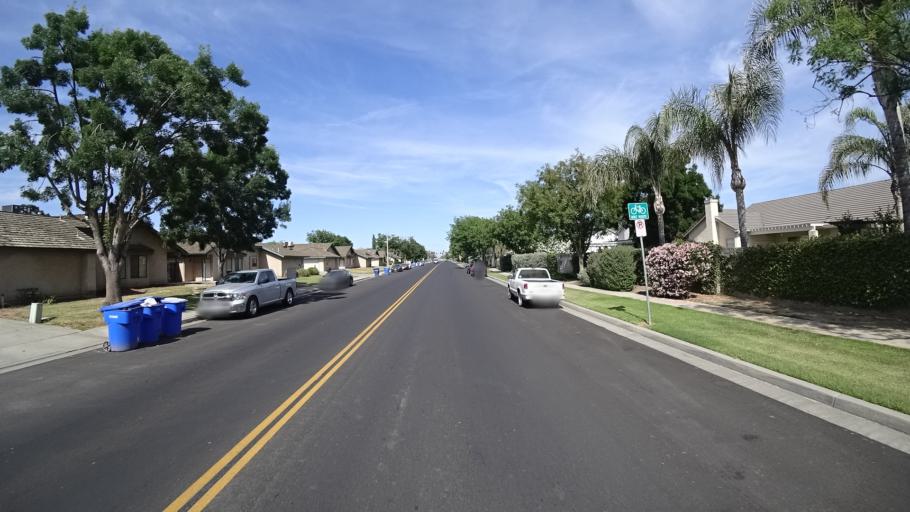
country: US
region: California
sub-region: Kings County
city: Hanford
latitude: 36.3573
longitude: -119.6336
